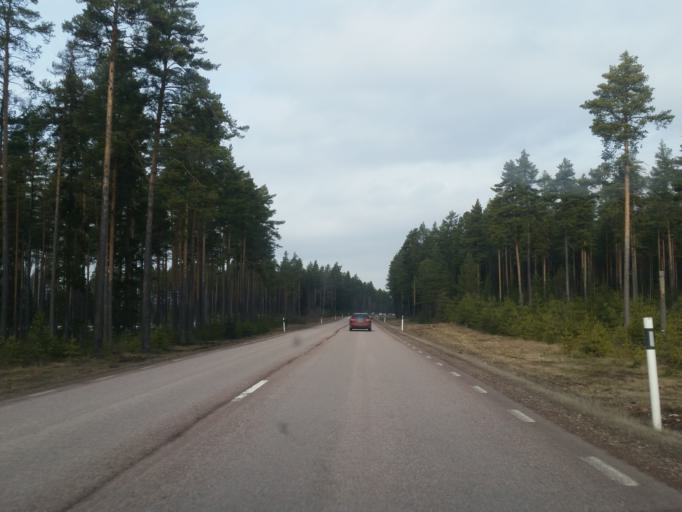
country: SE
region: Dalarna
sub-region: Mora Kommun
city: Mora
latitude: 60.9796
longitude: 14.6917
